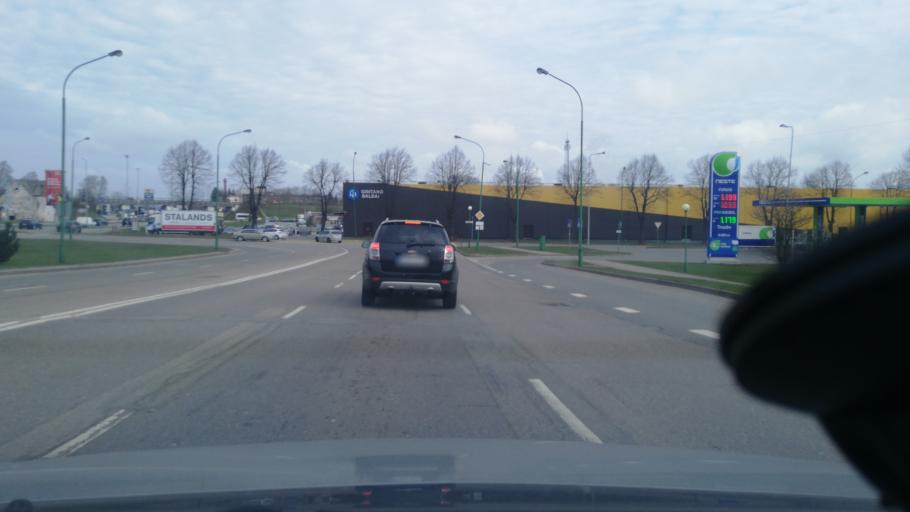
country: LT
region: Klaipedos apskritis
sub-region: Klaipeda
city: Klaipeda
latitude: 55.7174
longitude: 21.1506
